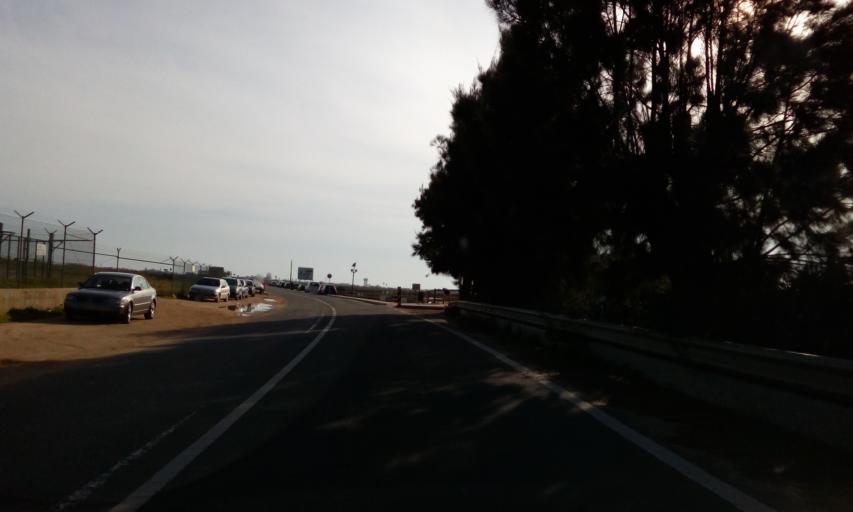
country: PT
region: Faro
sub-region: Faro
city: Faro
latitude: 37.0173
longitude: -7.9882
